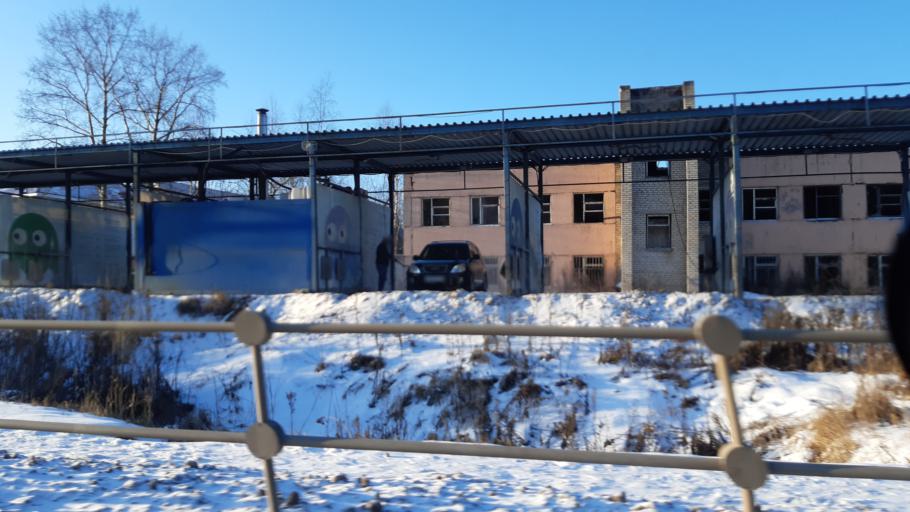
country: RU
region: Moskovskaya
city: Skoropuskovskiy
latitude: 56.3393
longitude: 38.1638
